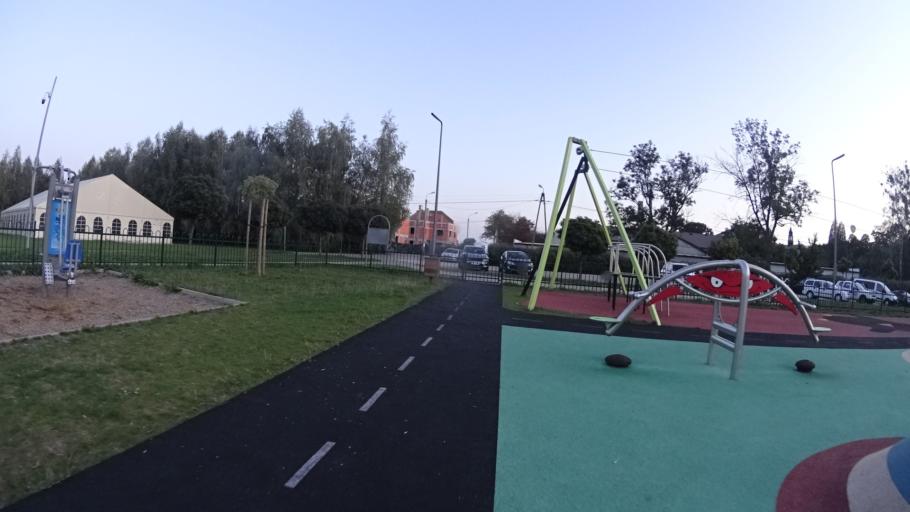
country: PL
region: Masovian Voivodeship
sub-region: Powiat warszawski zachodni
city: Ozarow Mazowiecki
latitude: 52.2151
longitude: 20.7776
